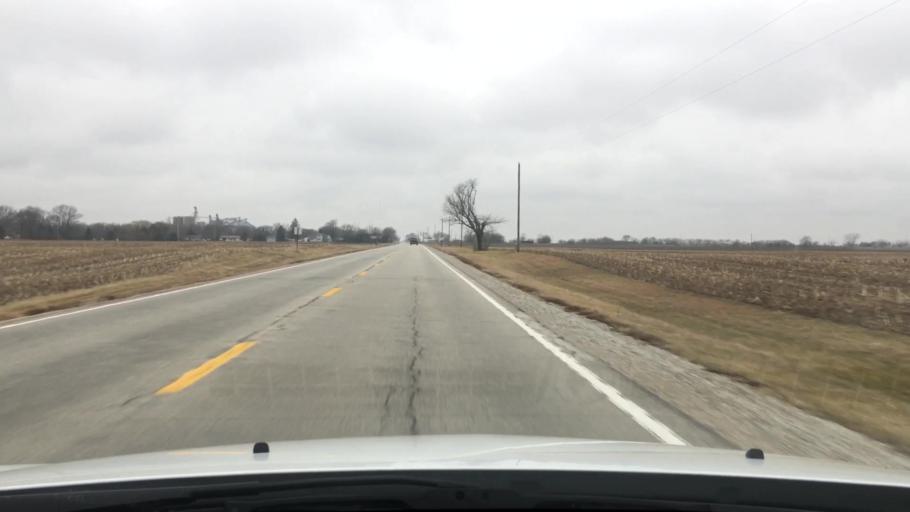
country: US
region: Illinois
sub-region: Iroquois County
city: Clifton
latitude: 40.8852
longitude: -87.9384
